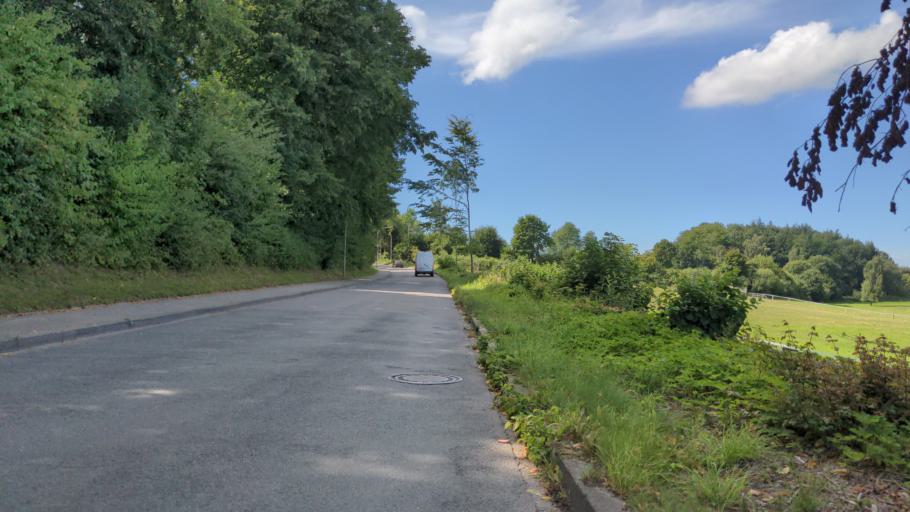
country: DE
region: Schleswig-Holstein
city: Malente
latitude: 54.1785
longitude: 10.5523
